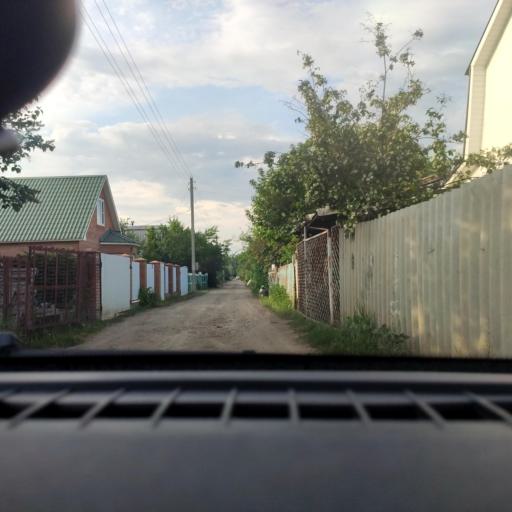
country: RU
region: Samara
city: Tol'yatti
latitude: 53.5937
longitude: 49.3206
